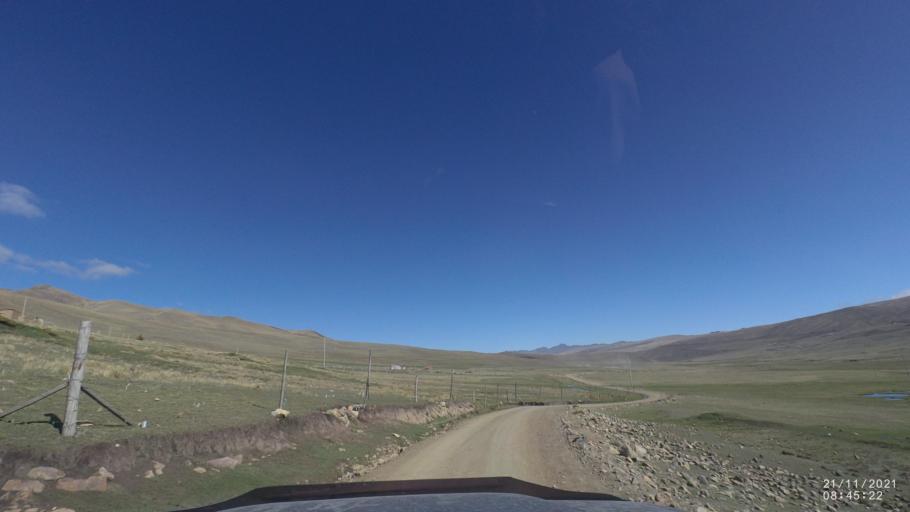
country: BO
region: Cochabamba
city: Cochabamba
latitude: -17.2492
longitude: -66.2318
